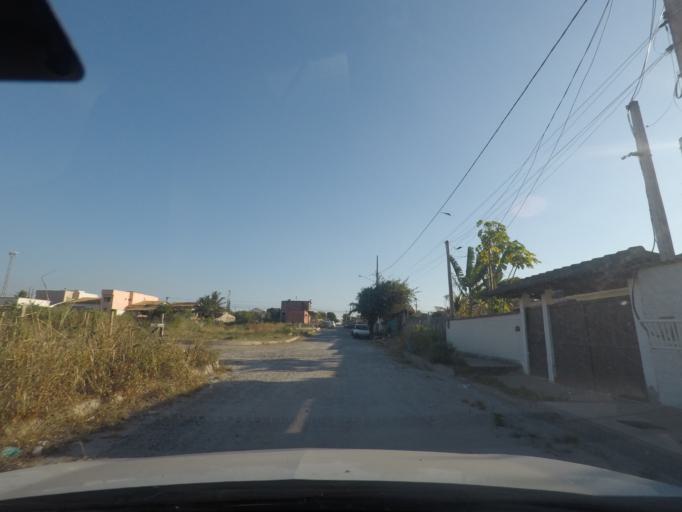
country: BR
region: Rio de Janeiro
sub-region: Marica
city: Marica
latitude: -22.9660
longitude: -42.9360
